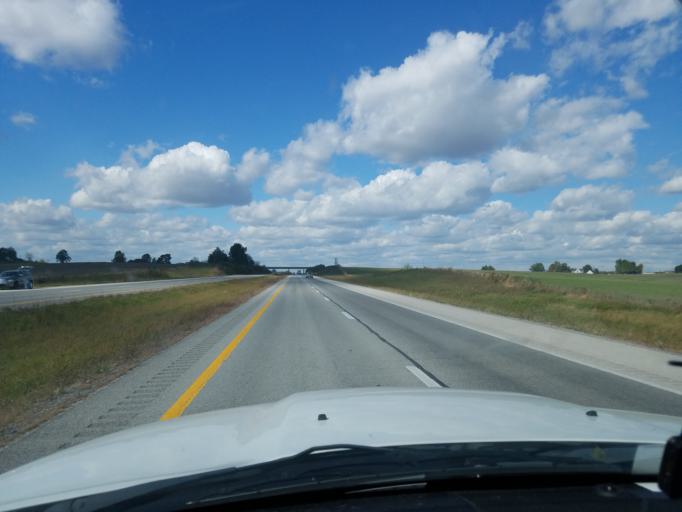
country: US
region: Kentucky
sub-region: Daviess County
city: Masonville
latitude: 37.6583
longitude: -87.0091
